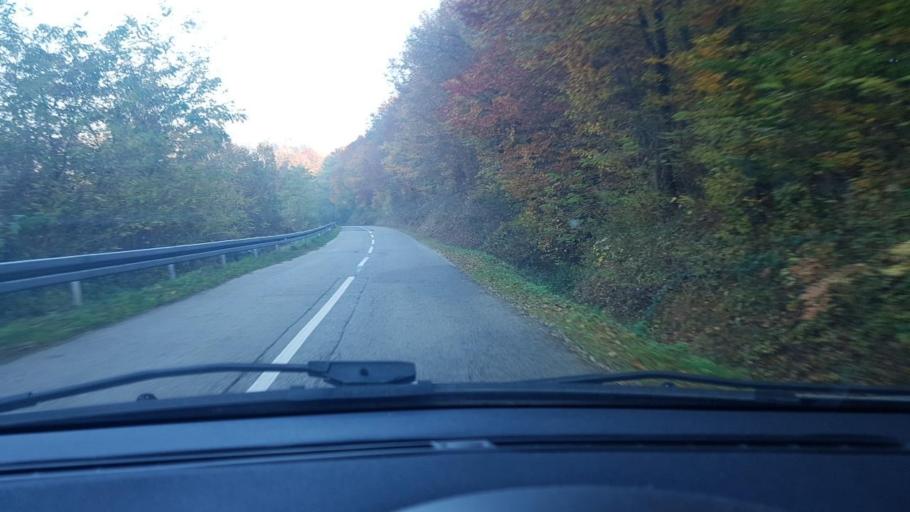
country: SI
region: Podcetrtek
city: Podcetrtek
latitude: 46.1857
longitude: 15.6403
